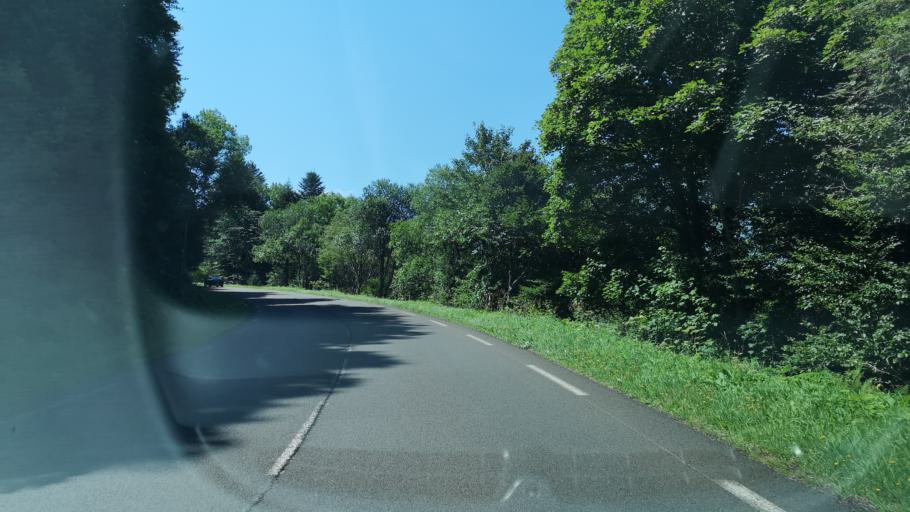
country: FR
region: Auvergne
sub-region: Departement du Puy-de-Dome
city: Mont-Dore
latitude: 45.5929
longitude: 2.8254
